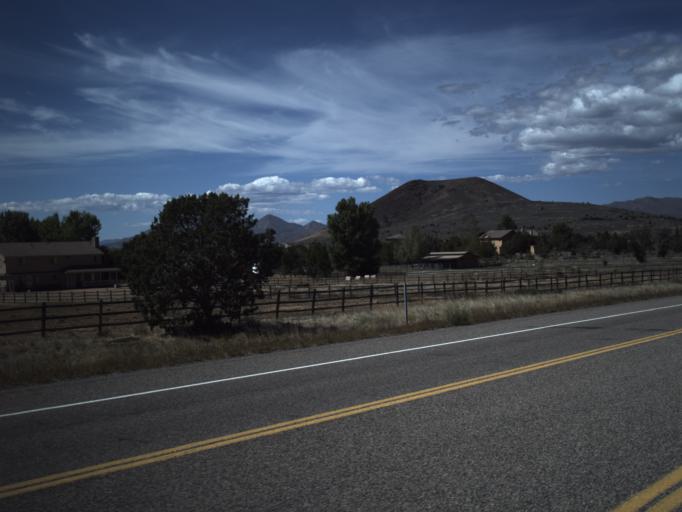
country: US
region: Utah
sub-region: Washington County
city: Ivins
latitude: 37.3035
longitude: -113.6691
